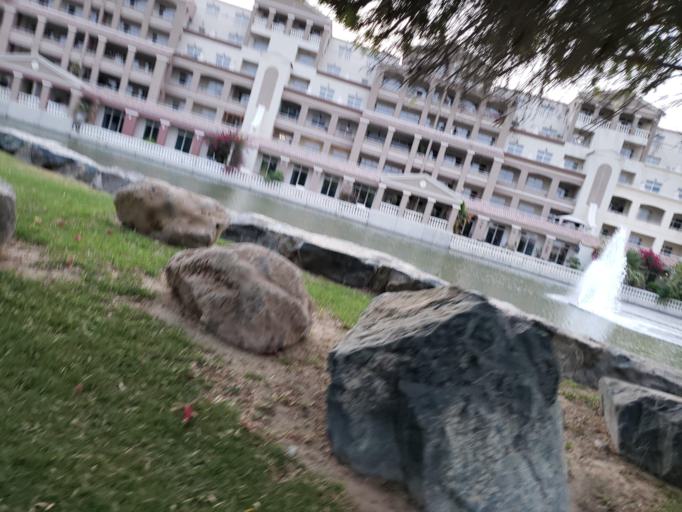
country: AE
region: Dubai
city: Dubai
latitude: 25.0403
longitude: 55.2309
